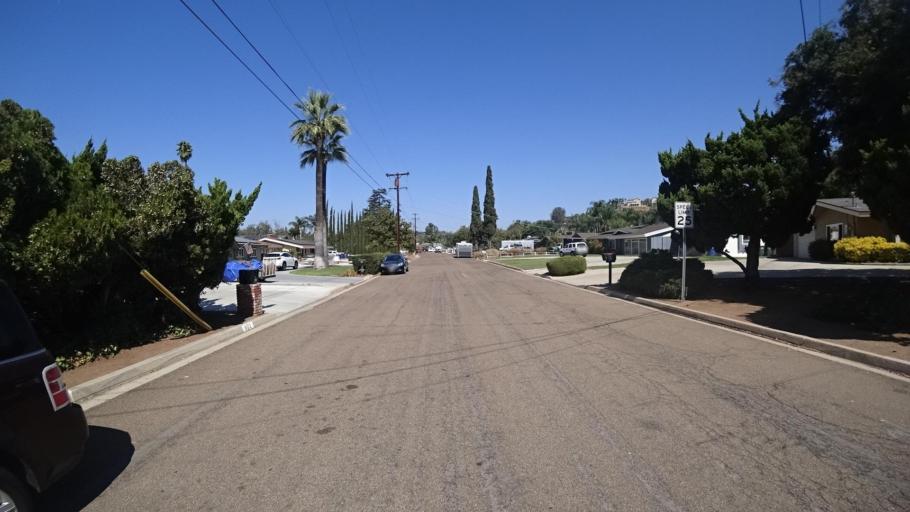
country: US
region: California
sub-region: San Diego County
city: Granite Hills
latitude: 32.8043
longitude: -116.9197
